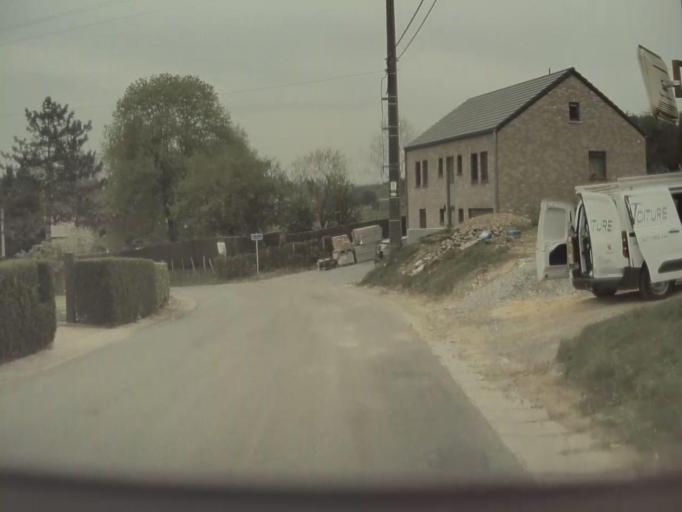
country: BE
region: Wallonia
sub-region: Province du Luxembourg
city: La Roche-en-Ardenne
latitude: 50.2337
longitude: 5.6206
